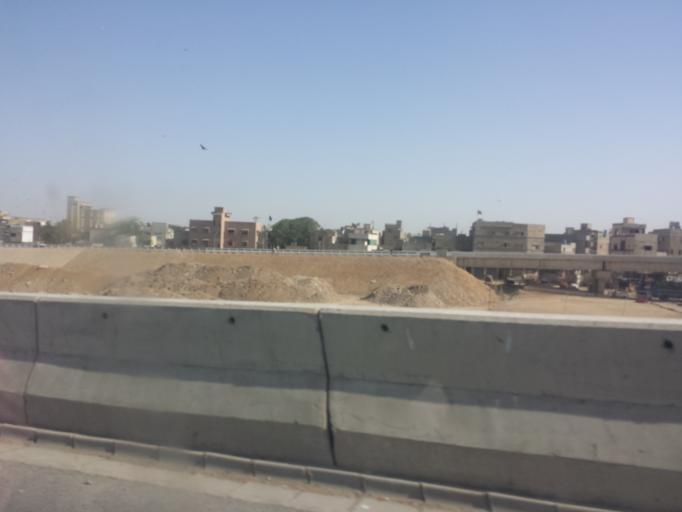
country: PK
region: Sindh
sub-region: Karachi District
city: Karachi
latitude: 24.8926
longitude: 67.0420
